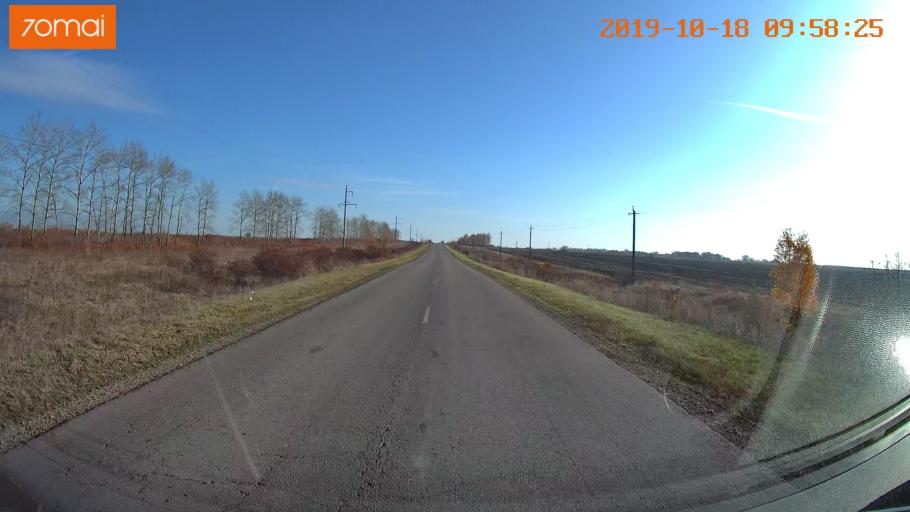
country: RU
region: Tula
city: Kurkino
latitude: 53.3749
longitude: 38.4396
